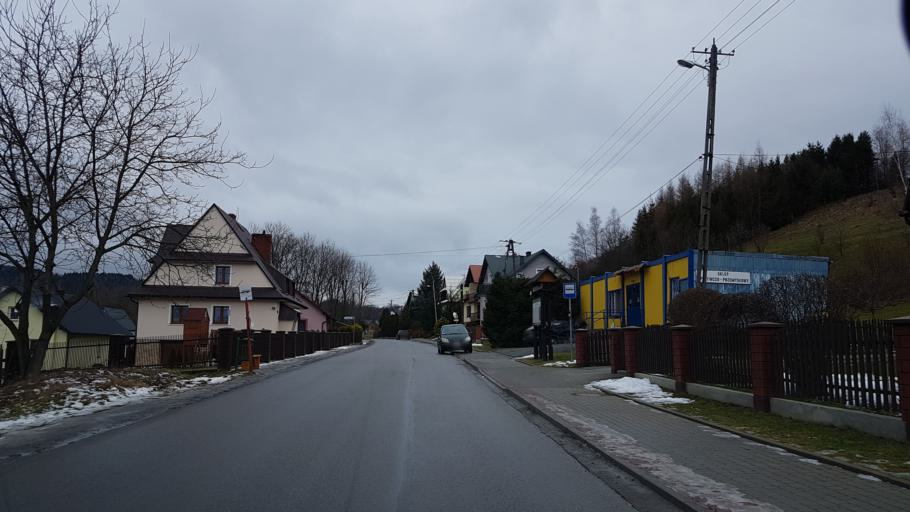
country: PL
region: Lesser Poland Voivodeship
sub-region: Powiat nowosadecki
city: Stary Sacz
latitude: 49.5116
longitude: 20.6114
